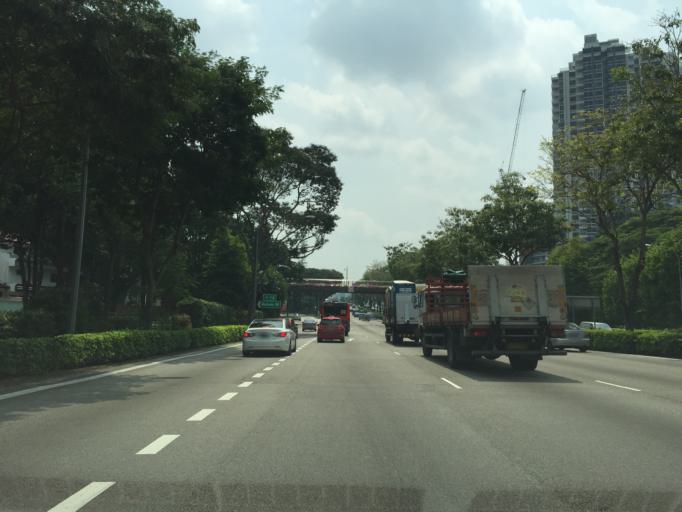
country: SG
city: Singapore
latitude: 1.3176
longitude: 103.8492
